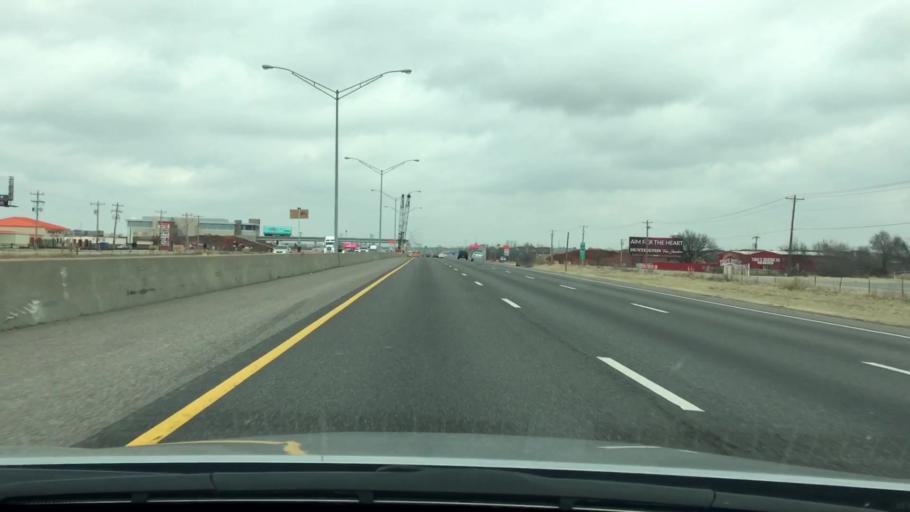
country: US
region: Oklahoma
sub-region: Cleveland County
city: Moore
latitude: 35.3017
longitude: -97.4899
